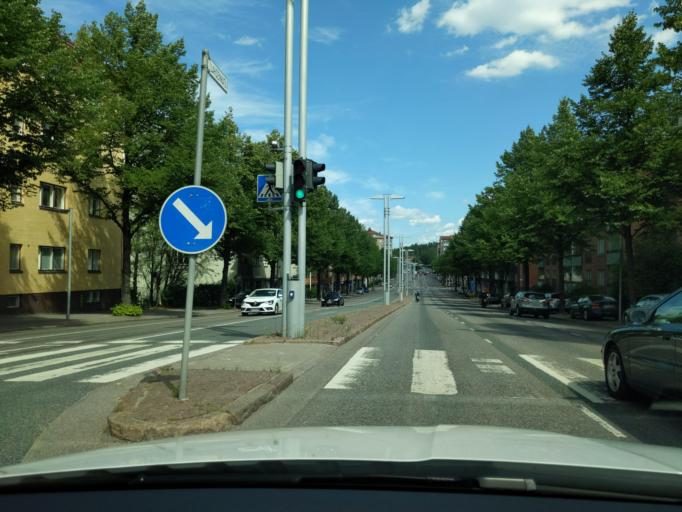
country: FI
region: Paijanne Tavastia
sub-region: Lahti
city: Lahti
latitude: 60.9871
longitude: 25.6560
